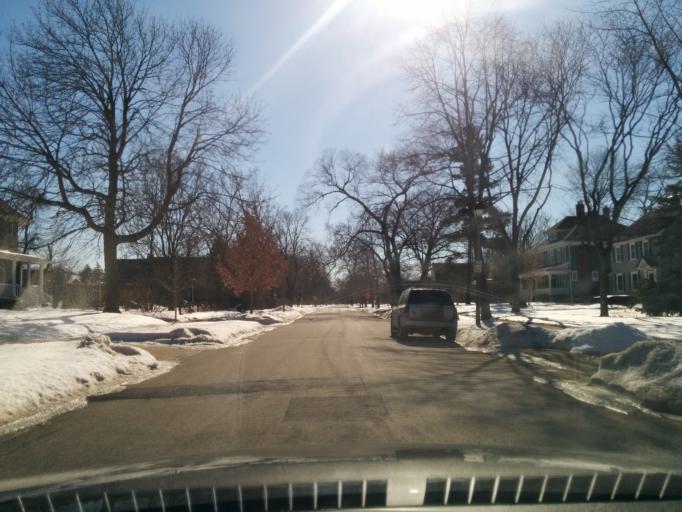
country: US
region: Illinois
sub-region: DuPage County
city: Elmhurst
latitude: 41.8957
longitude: -87.9384
